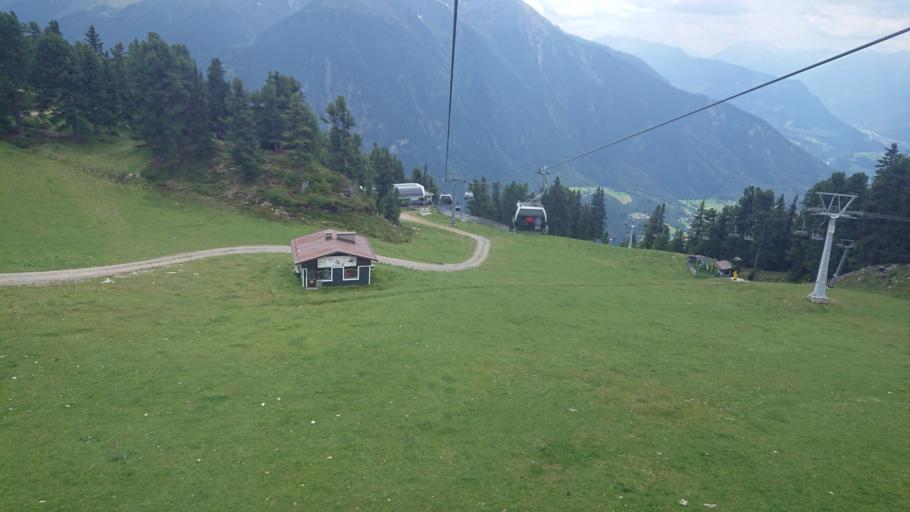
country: AT
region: Tyrol
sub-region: Politischer Bezirk Imst
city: Oetz
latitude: 47.2116
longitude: 10.9307
